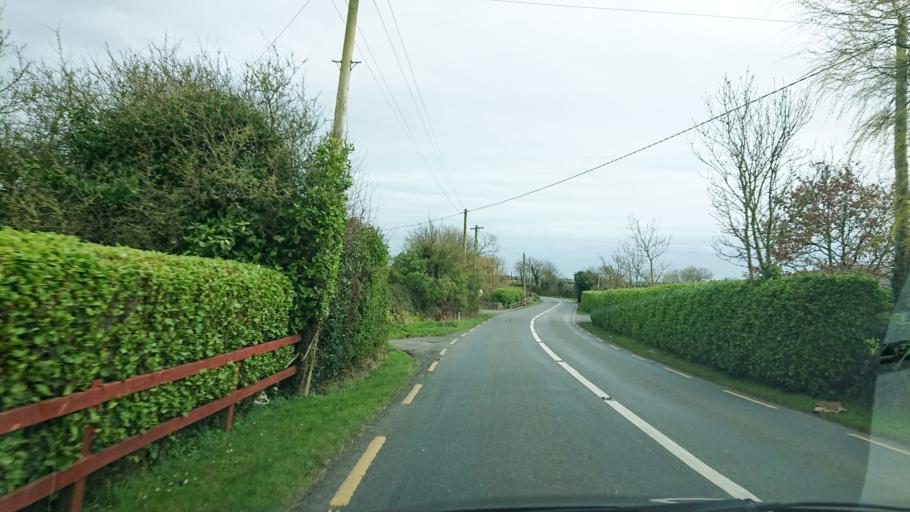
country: IE
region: Munster
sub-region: Waterford
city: Tra Mhor
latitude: 52.1802
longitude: -7.0745
